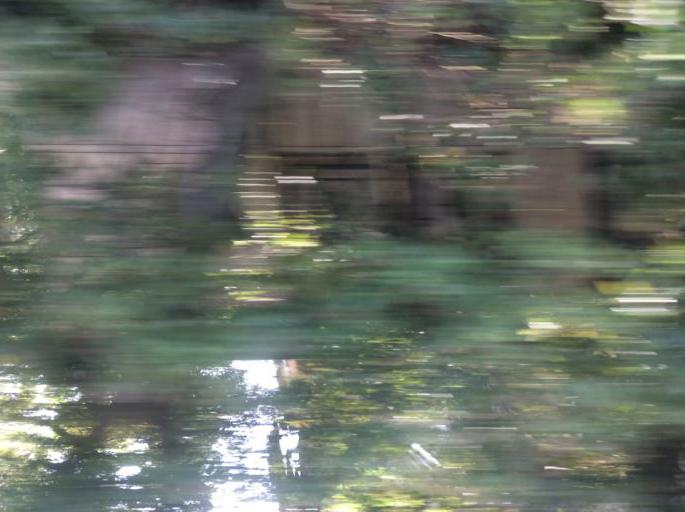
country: TW
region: Taipei
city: Taipei
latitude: 25.1339
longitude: 121.5459
